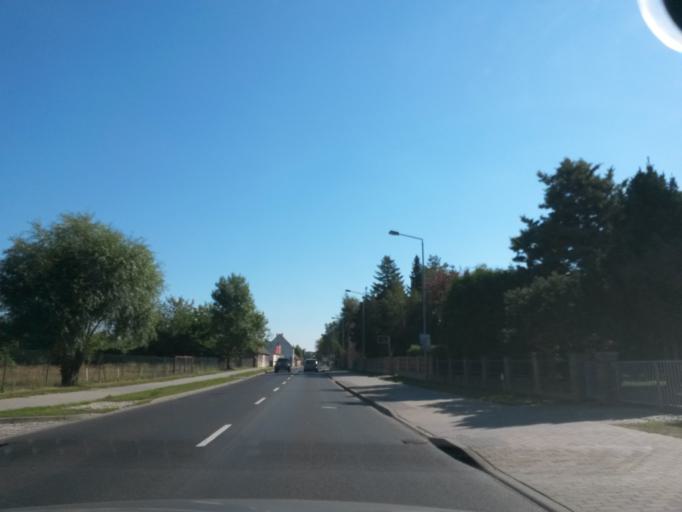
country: DE
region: Brandenburg
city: Prenzlau
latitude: 53.3081
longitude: 13.8356
